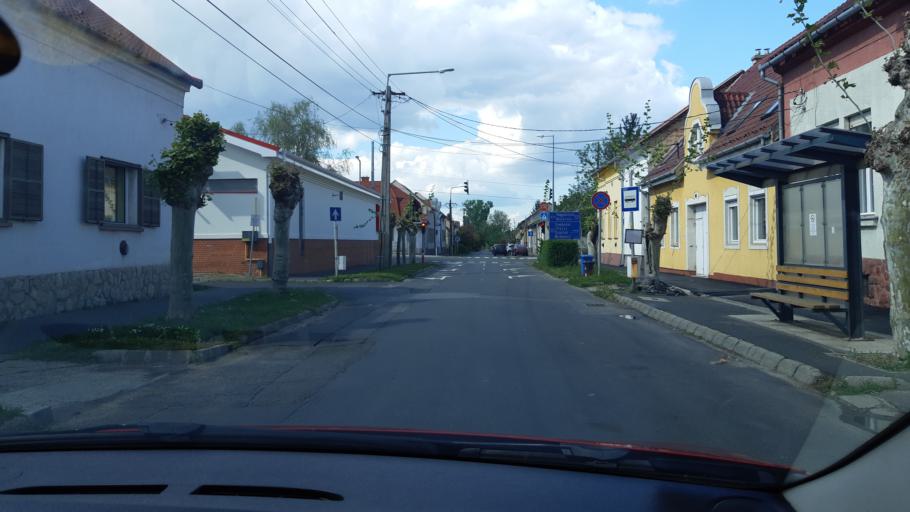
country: HU
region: Somogy
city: Kaposvar
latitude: 46.3644
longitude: 17.7972
